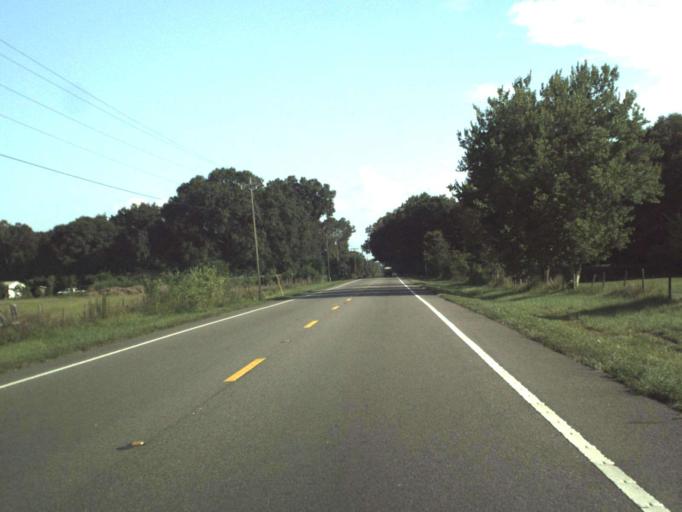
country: US
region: Florida
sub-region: Lake County
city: Groveland
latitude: 28.4303
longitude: -81.8327
